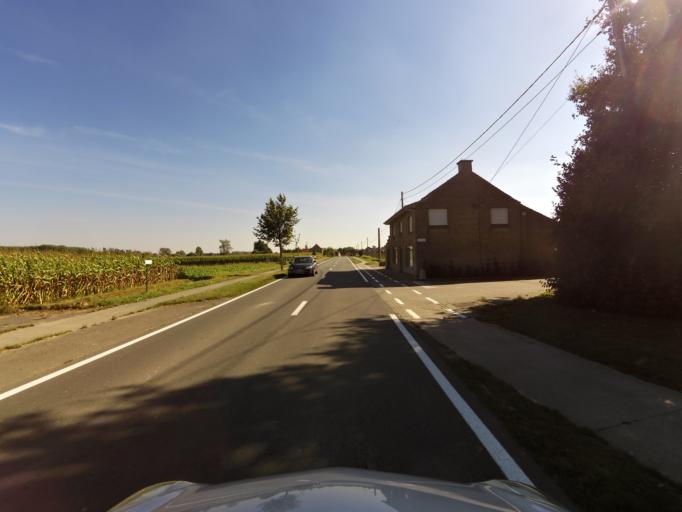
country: BE
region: Flanders
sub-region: Provincie West-Vlaanderen
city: Poperinge
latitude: 50.9156
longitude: 2.7355
